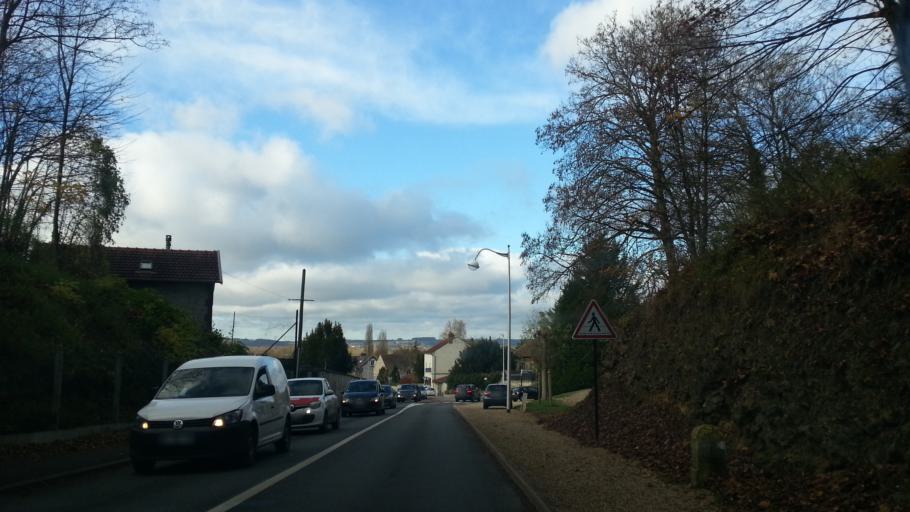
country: FR
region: Picardie
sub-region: Departement de l'Oise
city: Gouvieux
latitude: 49.1879
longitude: 2.4285
